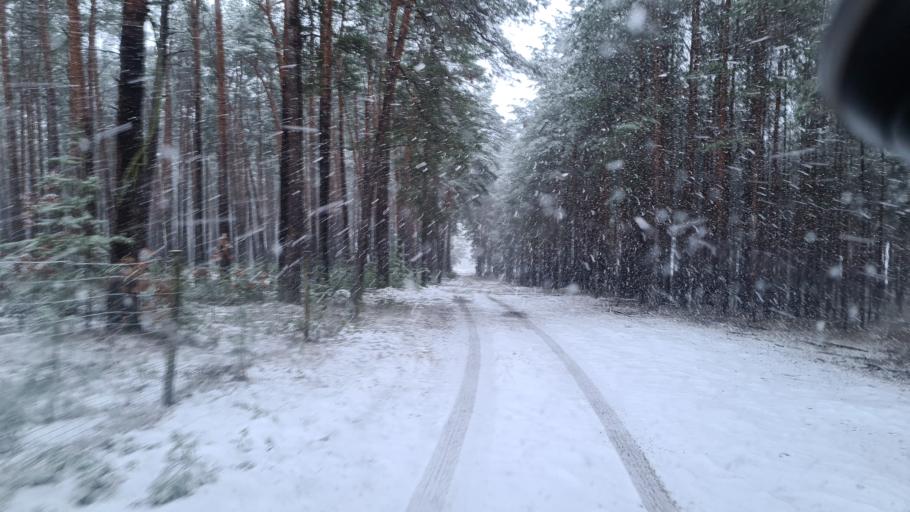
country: DE
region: Brandenburg
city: Schenkendobern
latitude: 51.9046
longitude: 14.5998
